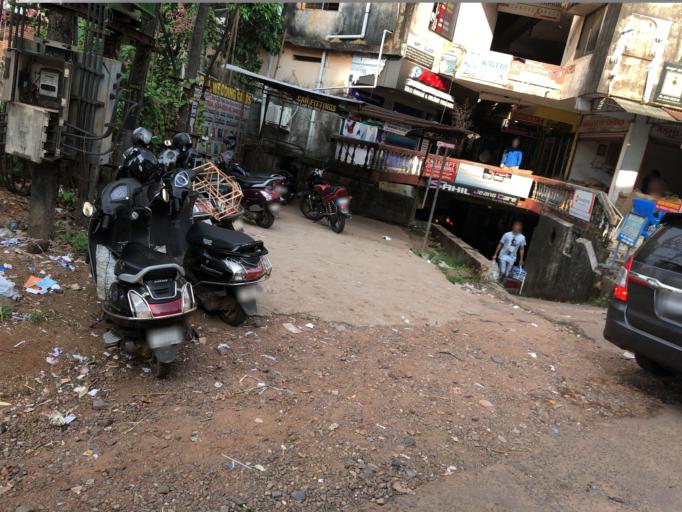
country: IN
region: Karnataka
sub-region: Dakshina Kannada
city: Mangalore
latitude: 12.8627
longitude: 74.8359
